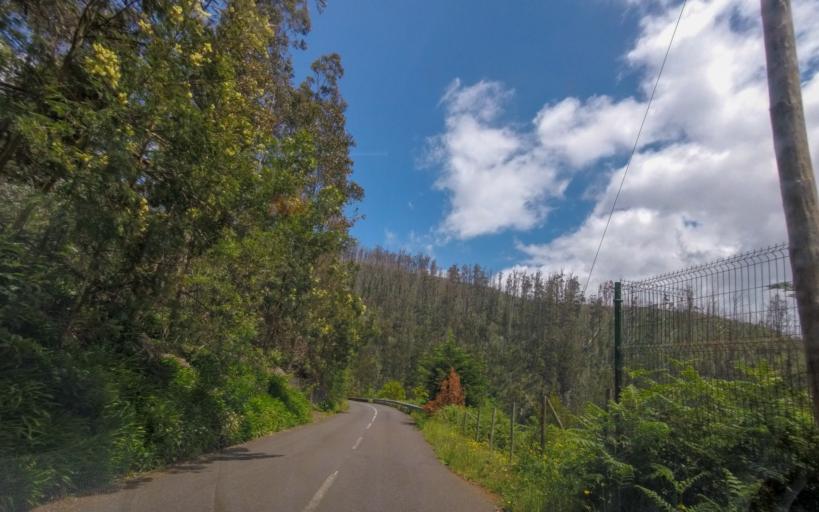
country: PT
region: Madeira
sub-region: Funchal
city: Nossa Senhora do Monte
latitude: 32.6798
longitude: -16.8829
